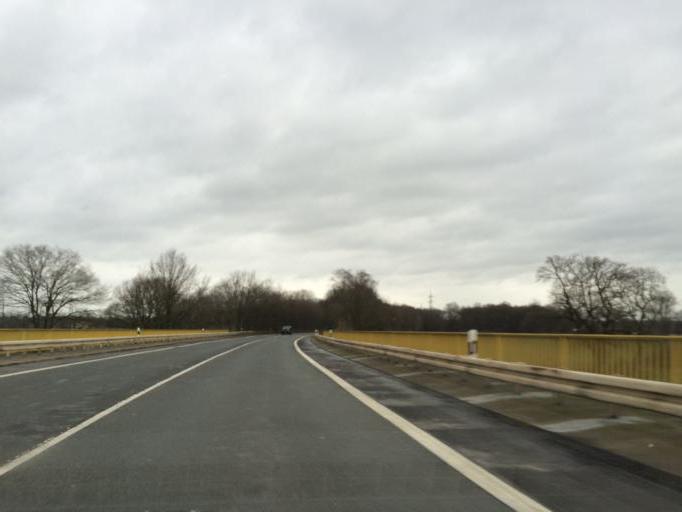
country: DE
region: North Rhine-Westphalia
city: Marl
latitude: 51.6911
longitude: 7.0663
